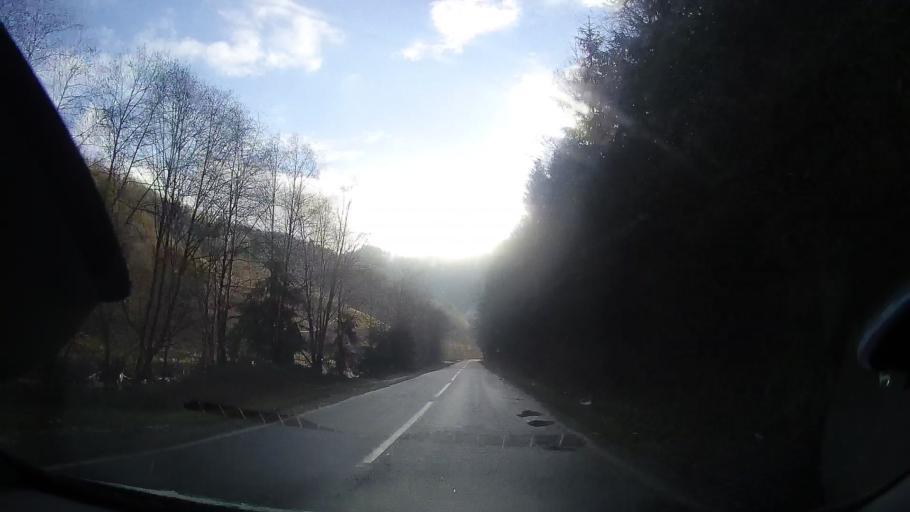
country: RO
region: Alba
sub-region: Comuna Vadu Motilor
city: Vadu Motilor
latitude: 46.4204
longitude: 22.9655
